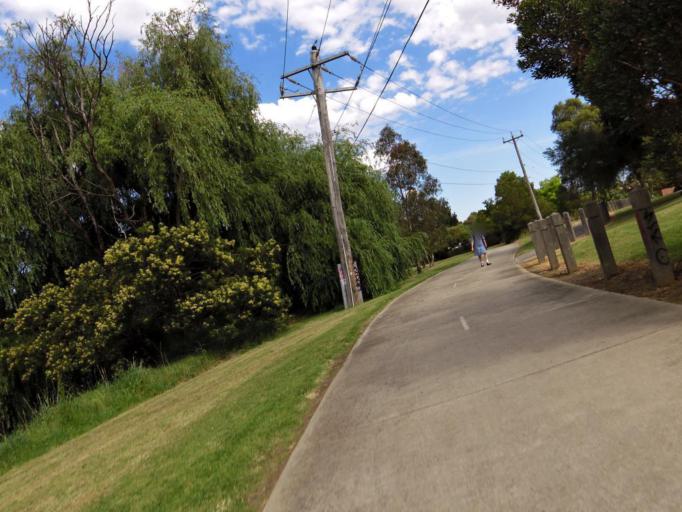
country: AU
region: Victoria
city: Macleod
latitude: -37.7353
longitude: 145.0796
